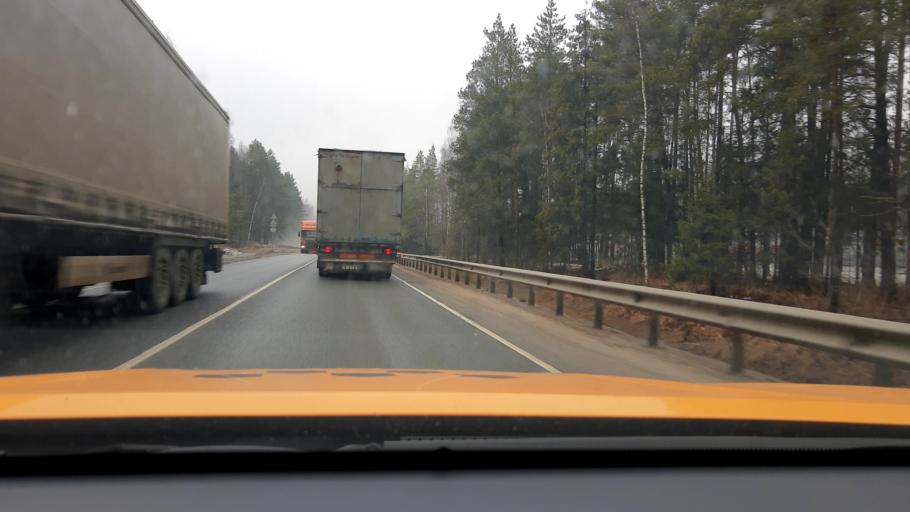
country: RU
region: Moskovskaya
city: Krasnoarmeysk
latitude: 56.0295
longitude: 38.2157
